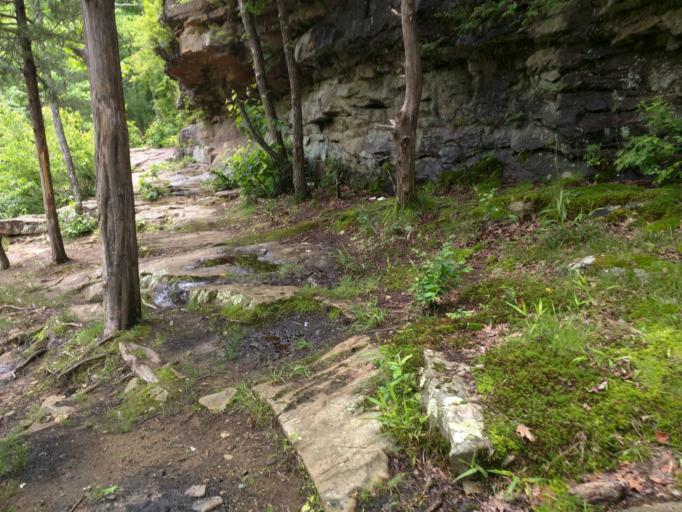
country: US
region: Arkansas
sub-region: Madison County
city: Huntsville
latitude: 35.9021
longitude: -93.5744
